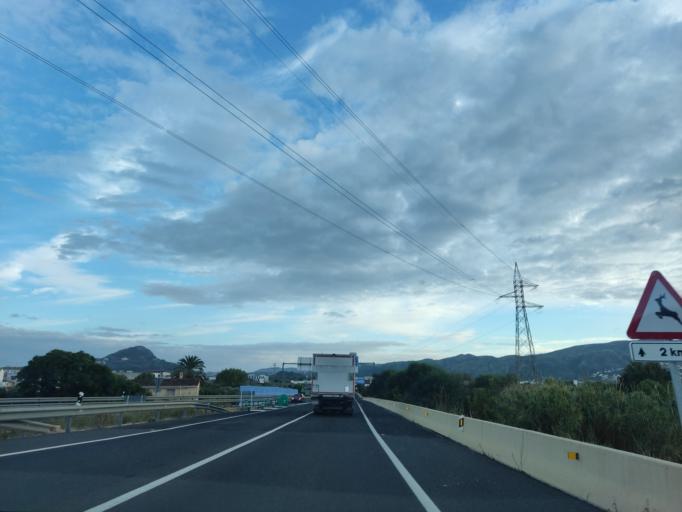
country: ES
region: Valencia
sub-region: Provincia de Alicante
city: Ondara
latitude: 38.8239
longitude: 0.0139
